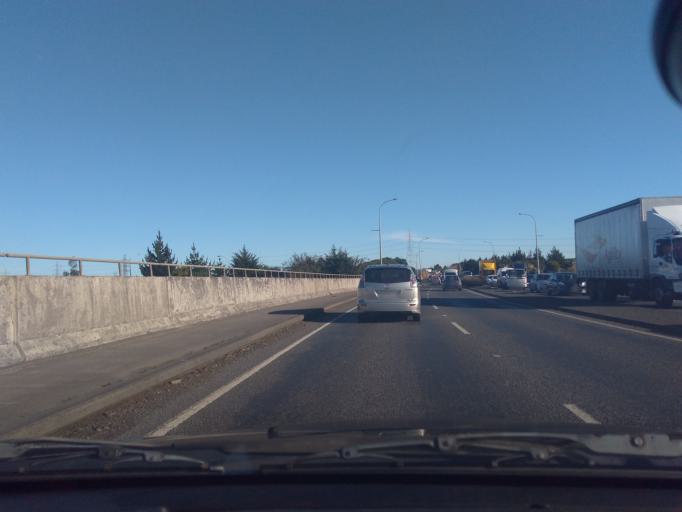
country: NZ
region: Auckland
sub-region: Auckland
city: Manukau City
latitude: -36.9458
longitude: 174.8617
